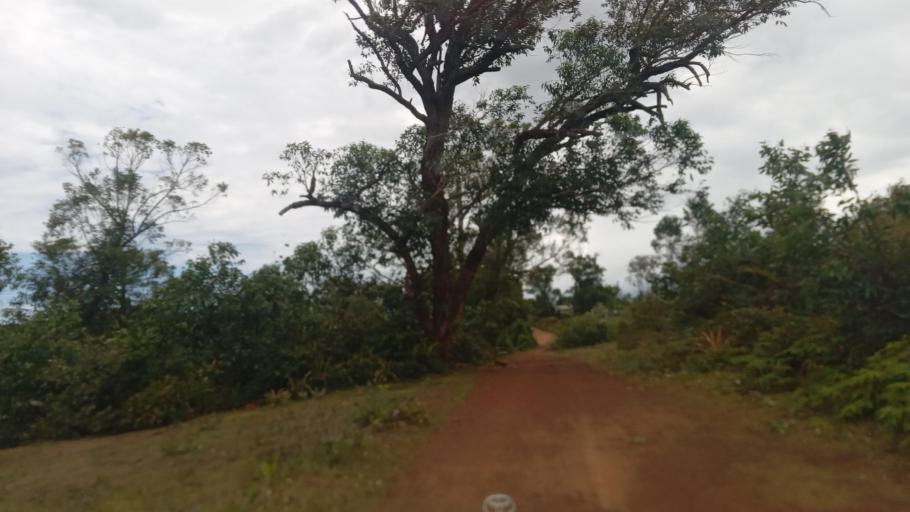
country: MG
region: Atsimo-Atsinanana
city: Vohipaho
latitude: -23.6189
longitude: 47.5802
